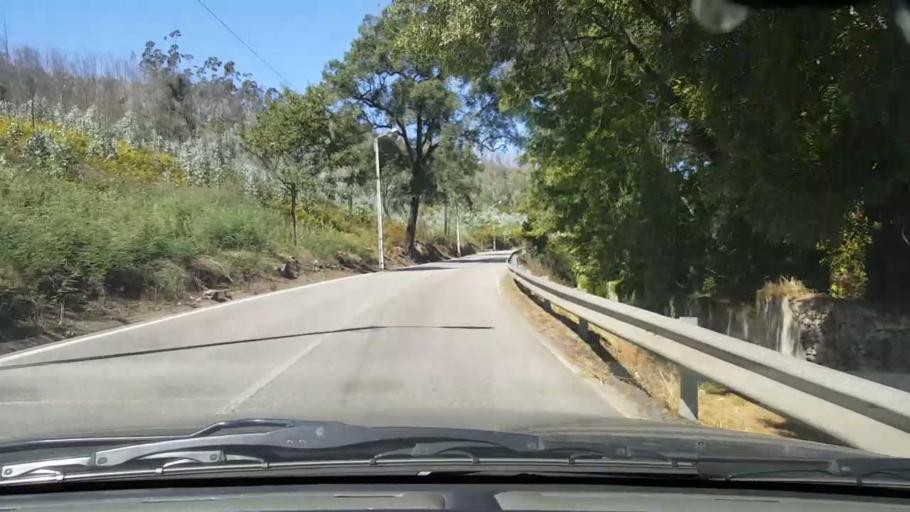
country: PT
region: Braga
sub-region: Vila Nova de Famalicao
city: Ribeirao
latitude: 41.3355
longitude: -8.6217
